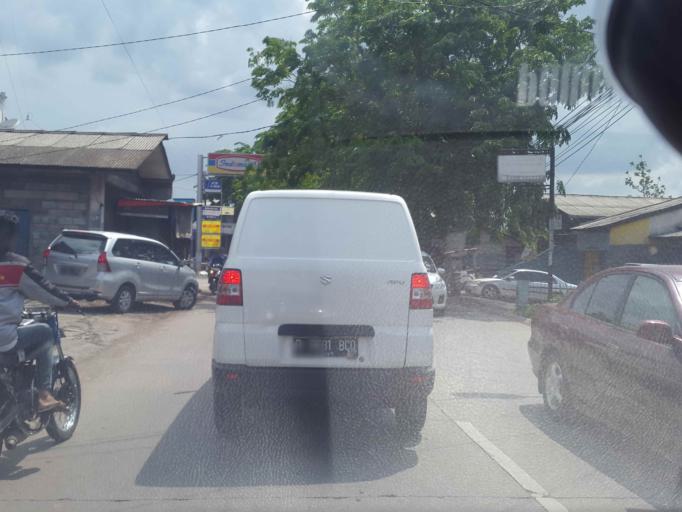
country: ID
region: West Java
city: Bekasi
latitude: -6.2883
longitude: 106.9673
